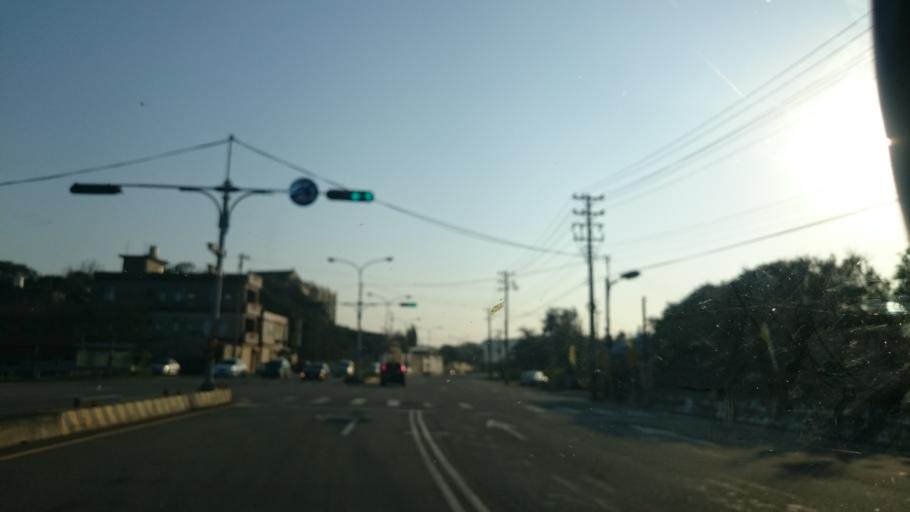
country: TW
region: Taiwan
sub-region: Miaoli
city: Miaoli
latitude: 24.6075
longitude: 120.7837
